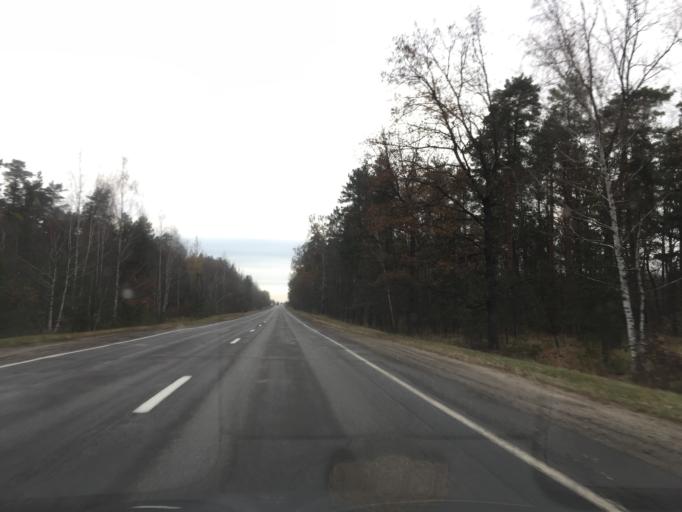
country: BY
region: Gomel
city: Gomel
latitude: 52.4064
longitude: 30.8290
